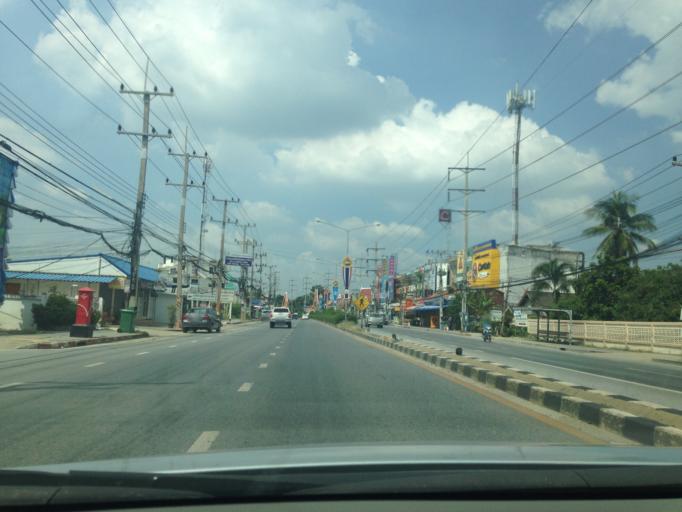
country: TH
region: Pathum Thani
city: Sam Khok
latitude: 14.0651
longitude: 100.5235
